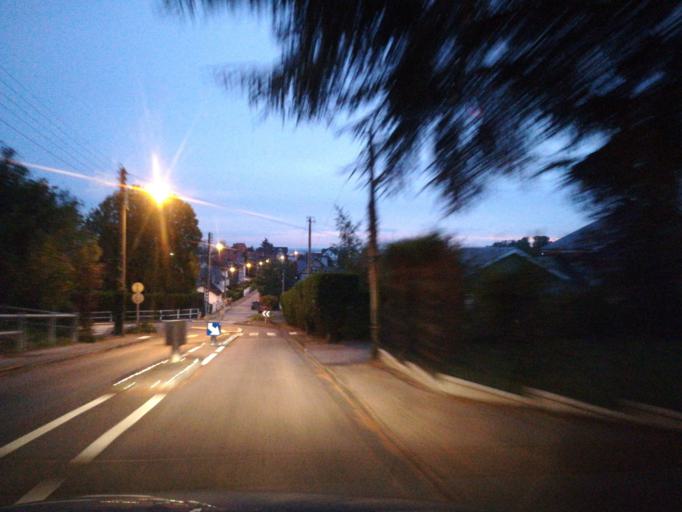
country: FR
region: Haute-Normandie
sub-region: Departement de la Seine-Maritime
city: Mont-Saint-Aignan
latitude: 49.4615
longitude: 1.0907
